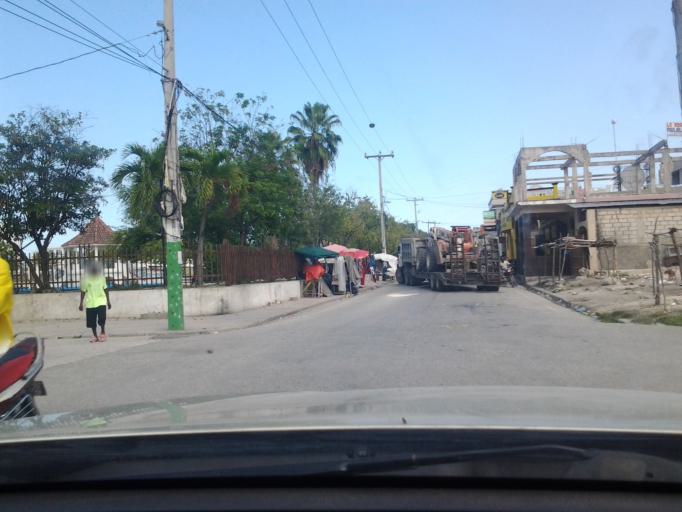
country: HT
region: Ouest
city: Tigwav
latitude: 18.4323
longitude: -72.8667
